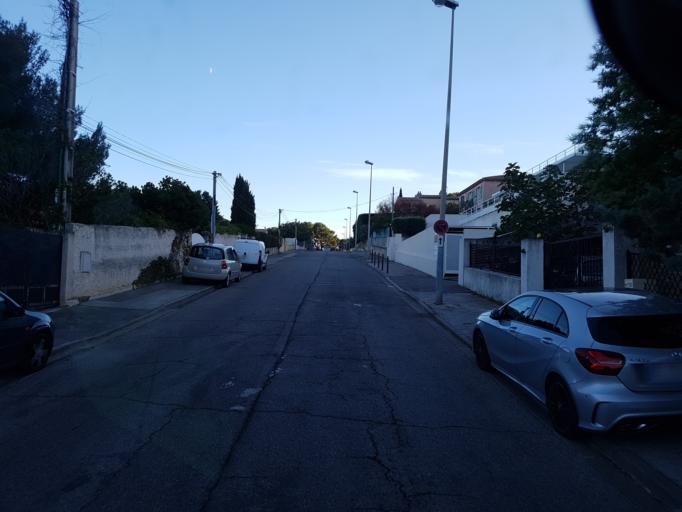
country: FR
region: Provence-Alpes-Cote d'Azur
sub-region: Departement des Bouches-du-Rhone
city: La Ciotat
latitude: 43.1746
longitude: 5.5980
